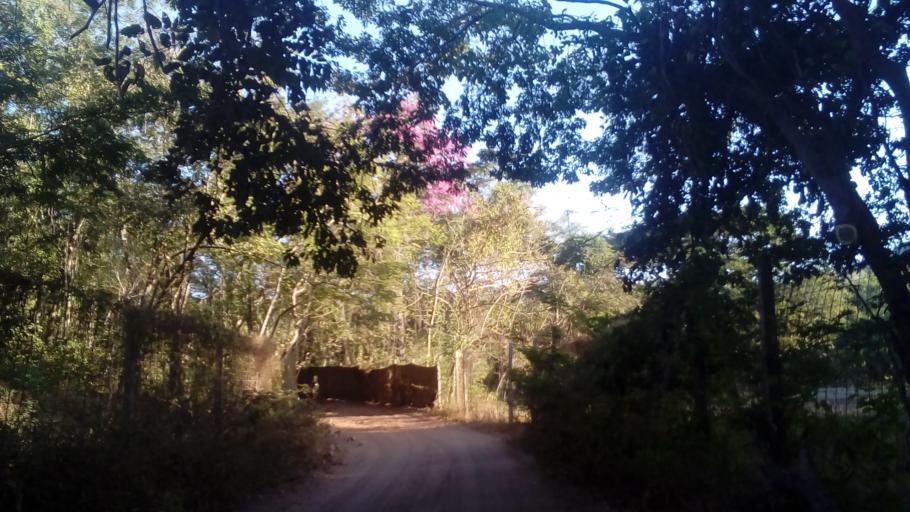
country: CR
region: Guanacaste
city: Sardinal
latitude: 10.3907
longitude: -85.8270
